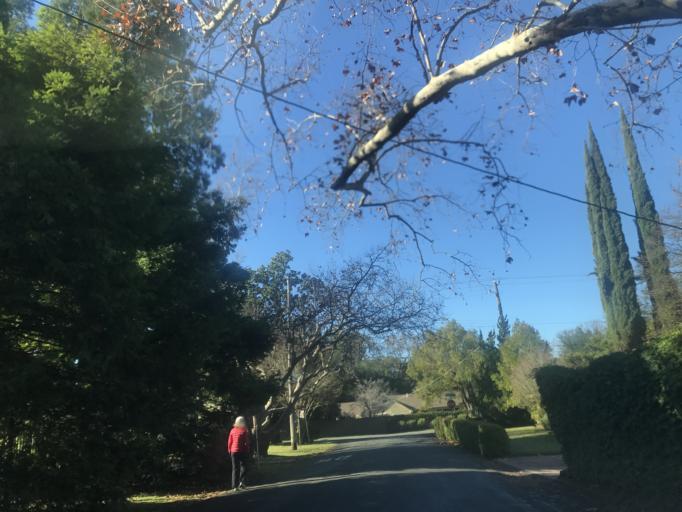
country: US
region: California
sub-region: Sacramento County
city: Sacramento
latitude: 38.5315
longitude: -121.5044
